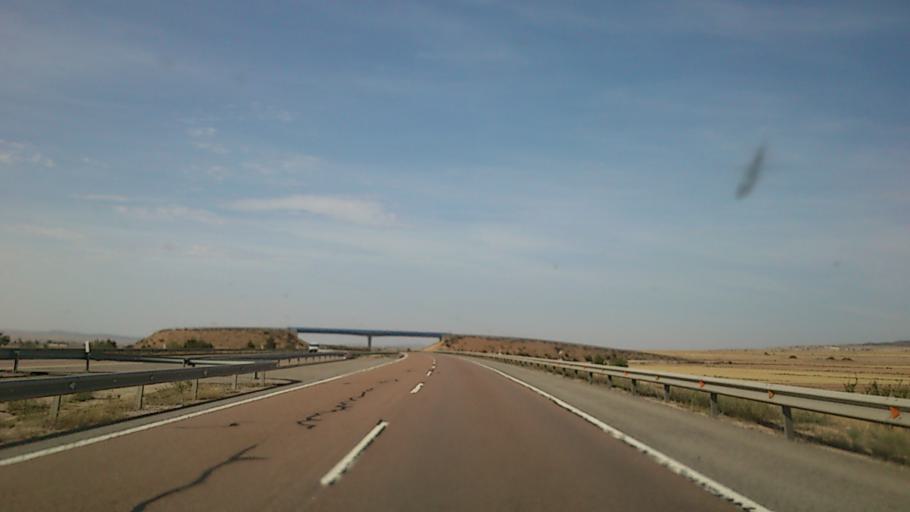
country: ES
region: Aragon
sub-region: Provincia de Teruel
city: Singra
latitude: 40.6761
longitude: -1.3139
